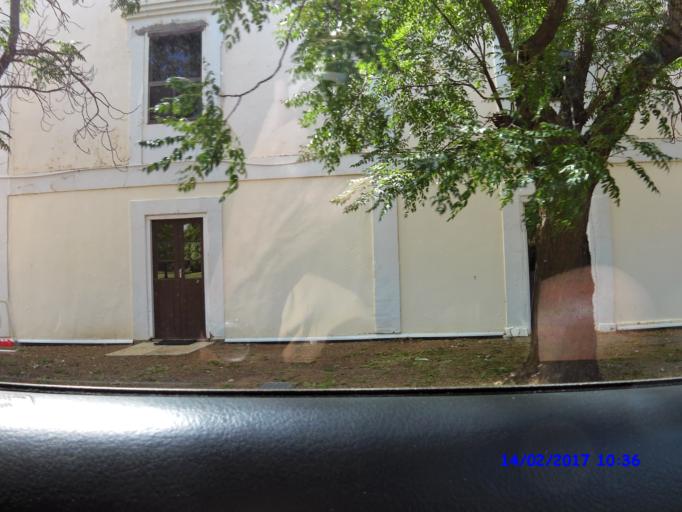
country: AU
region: Western Australia
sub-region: Moora
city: Moora
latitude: -30.9705
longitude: 116.2166
